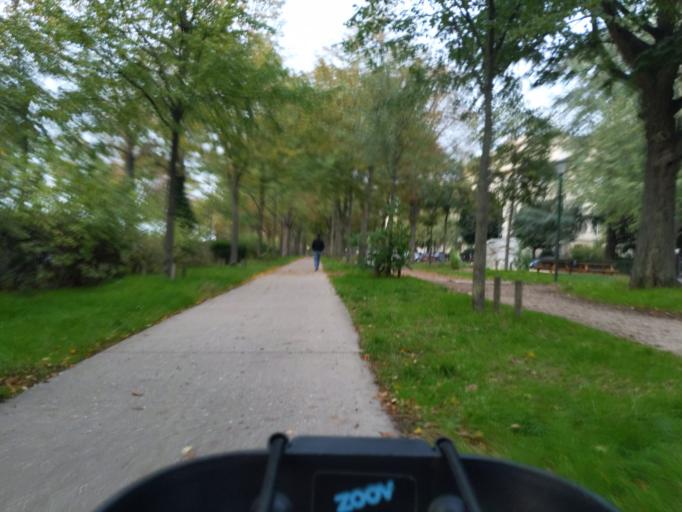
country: FR
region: Ile-de-France
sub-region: Departement des Hauts-de-Seine
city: Boulogne-Billancourt
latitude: 48.8507
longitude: 2.2589
